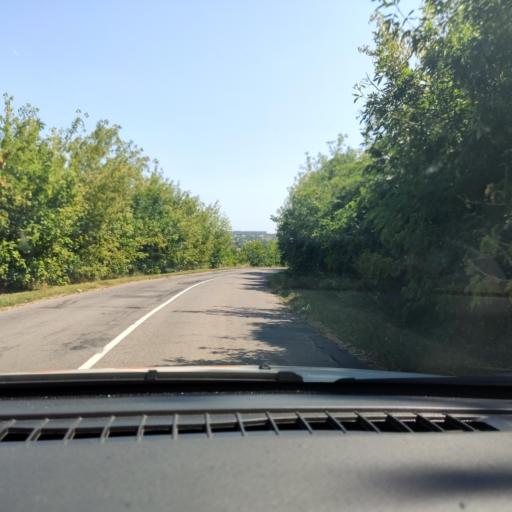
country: RU
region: Voronezj
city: Imeni Pervogo Maya
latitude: 50.7177
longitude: 39.3512
